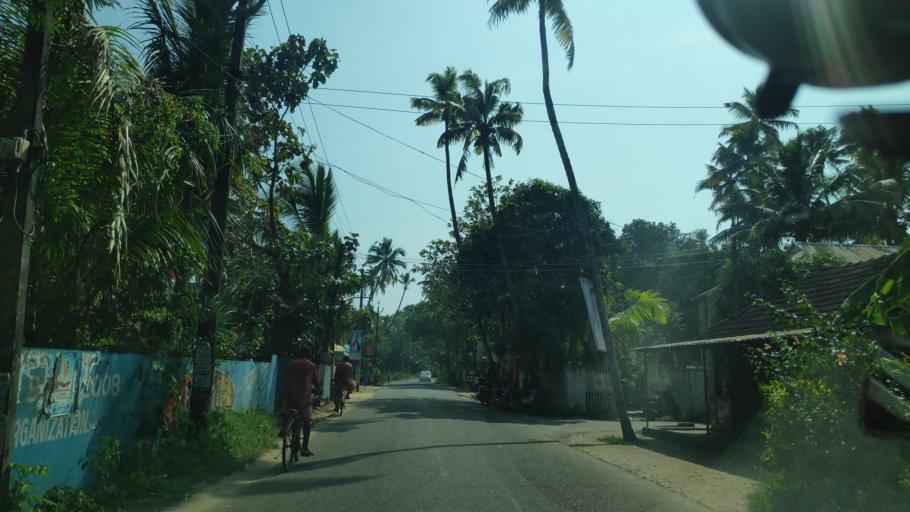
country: IN
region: Kerala
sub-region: Alappuzha
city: Vayalar
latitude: 9.6455
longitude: 76.2987
